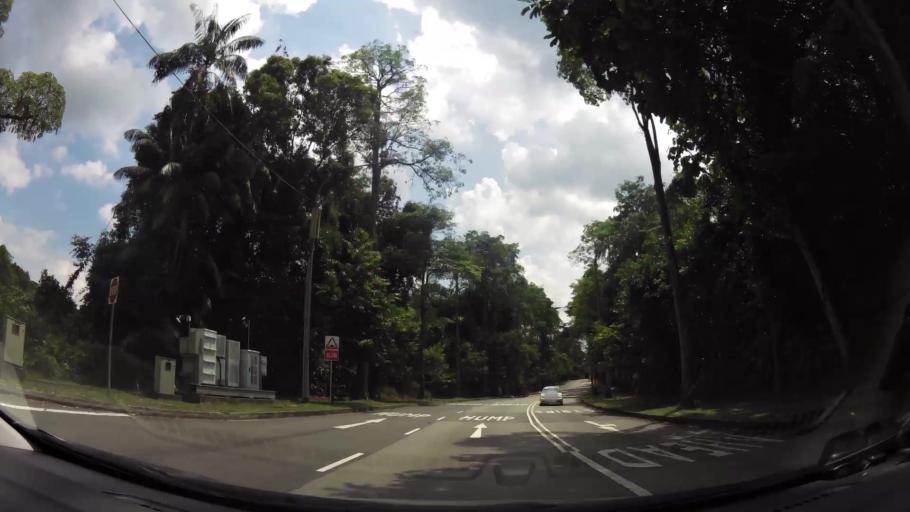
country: MY
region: Johor
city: Johor Bahru
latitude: 1.4070
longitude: 103.7846
